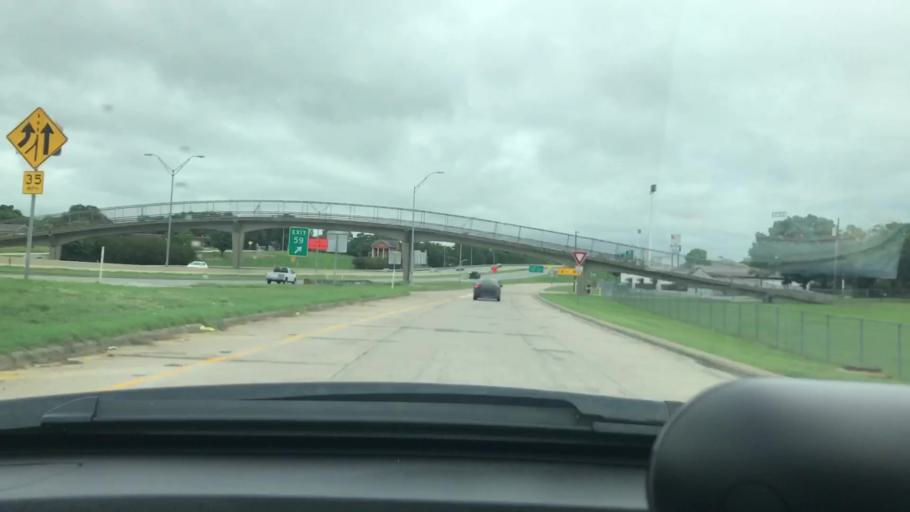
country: US
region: Texas
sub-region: Grayson County
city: Sherman
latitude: 33.6362
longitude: -96.6161
